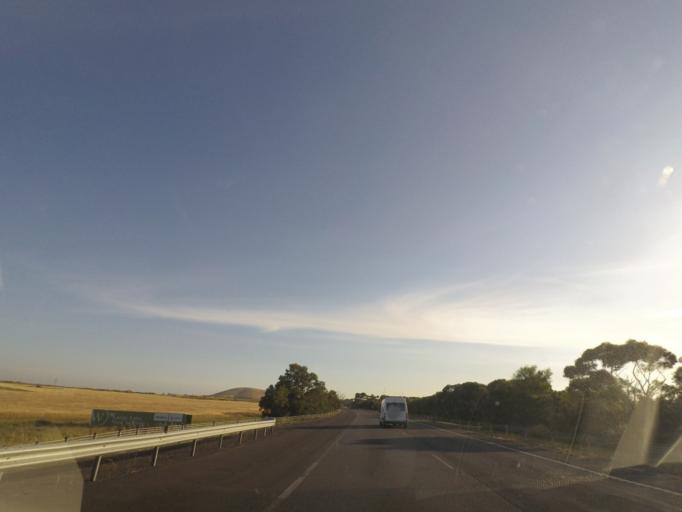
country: AU
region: Victoria
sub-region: Whittlesea
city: Whittlesea
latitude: -37.4313
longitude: 144.9834
